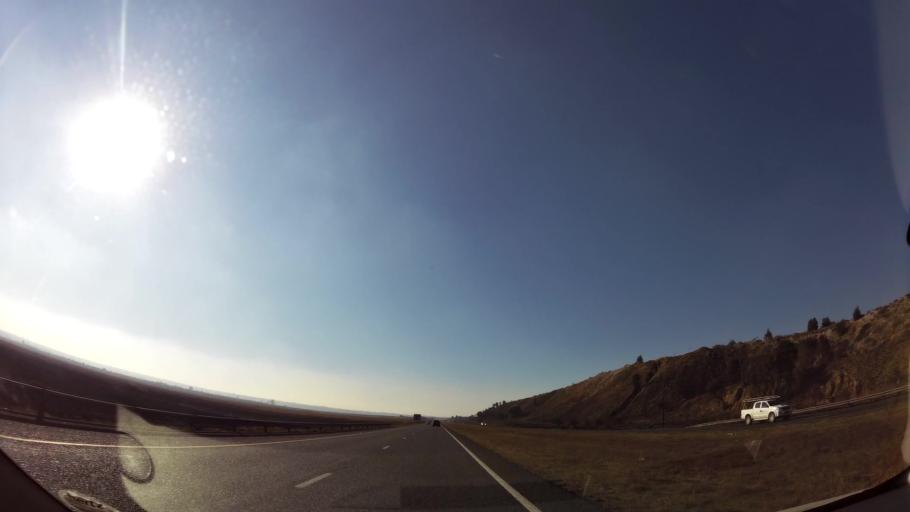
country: ZA
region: Mpumalanga
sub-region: Nkangala District Municipality
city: Witbank
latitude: -26.0208
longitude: 29.0175
